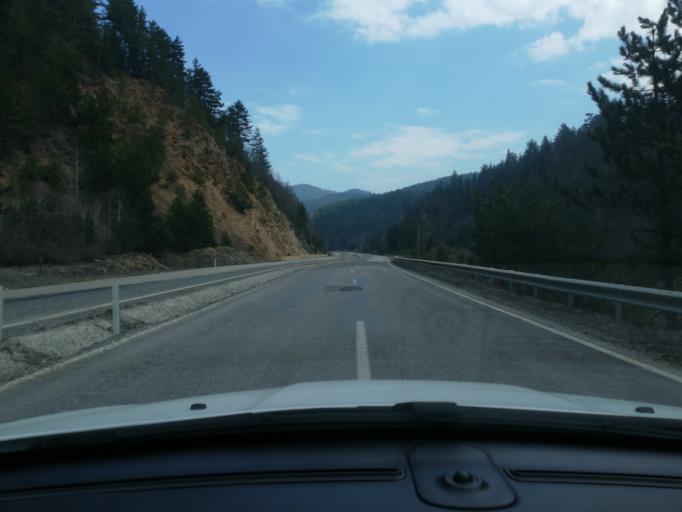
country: TR
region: Kastamonu
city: Kuzyaka
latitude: 41.1543
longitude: 33.7892
